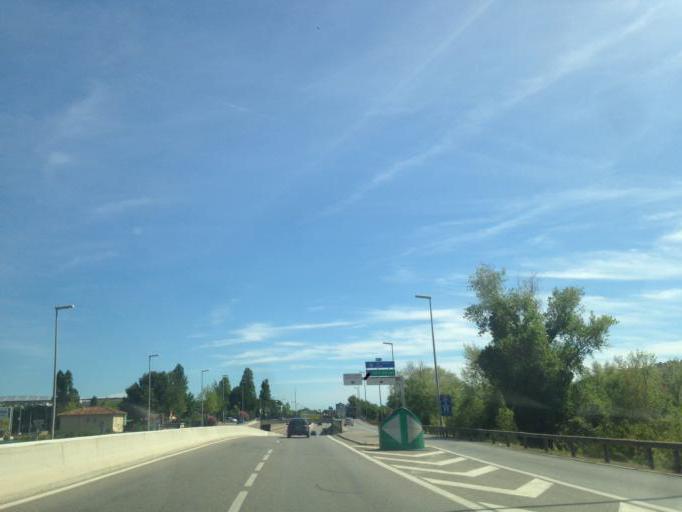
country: FR
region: Provence-Alpes-Cote d'Azur
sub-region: Departement des Alpes-Maritimes
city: La Gaude
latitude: 43.7122
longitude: 7.1874
